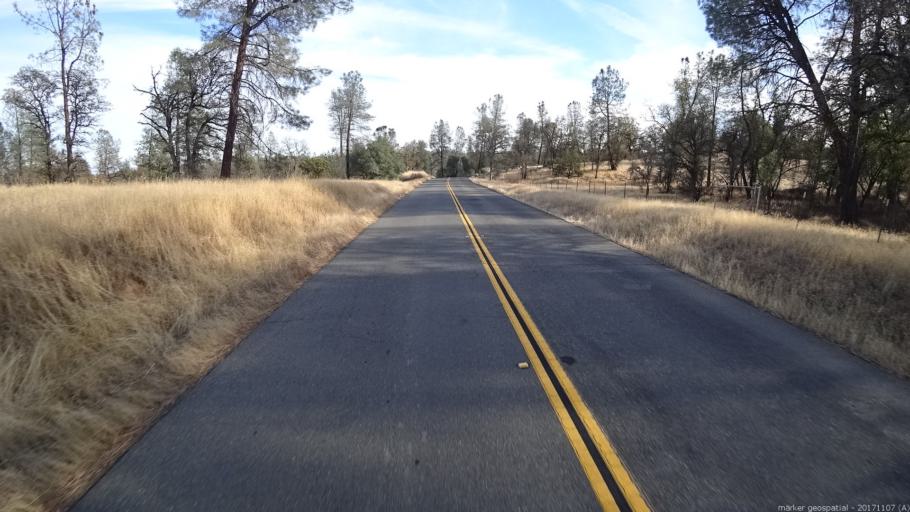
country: US
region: California
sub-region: Shasta County
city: Redding
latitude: 40.5103
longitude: -122.4499
